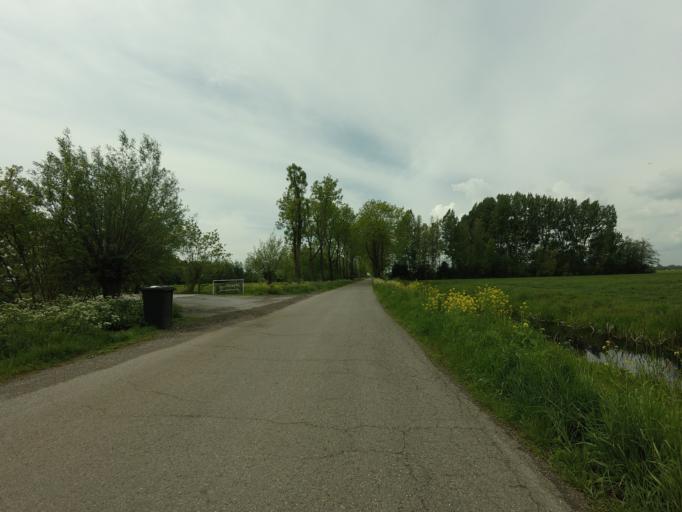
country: NL
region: Utrecht
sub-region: Gemeente Oudewater
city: Oudewater
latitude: 52.0047
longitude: 4.8533
